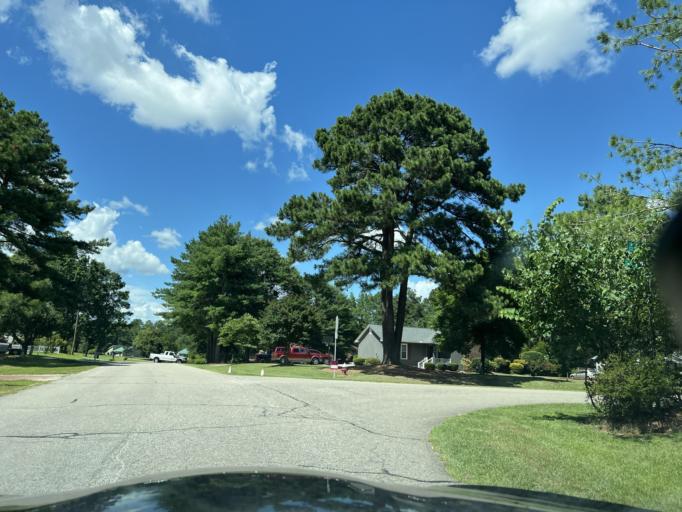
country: US
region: North Carolina
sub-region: Lee County
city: Sanford
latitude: 35.4338
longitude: -79.1637
